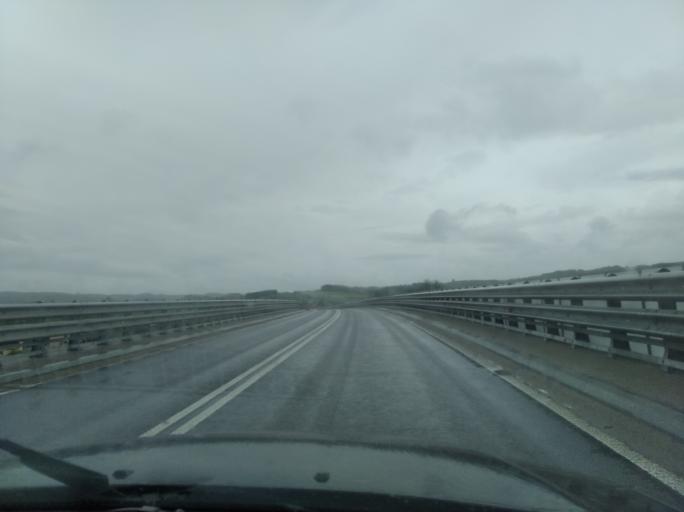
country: PL
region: Subcarpathian Voivodeship
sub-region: Powiat strzyzowski
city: Czudec
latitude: 49.9385
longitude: 21.8242
